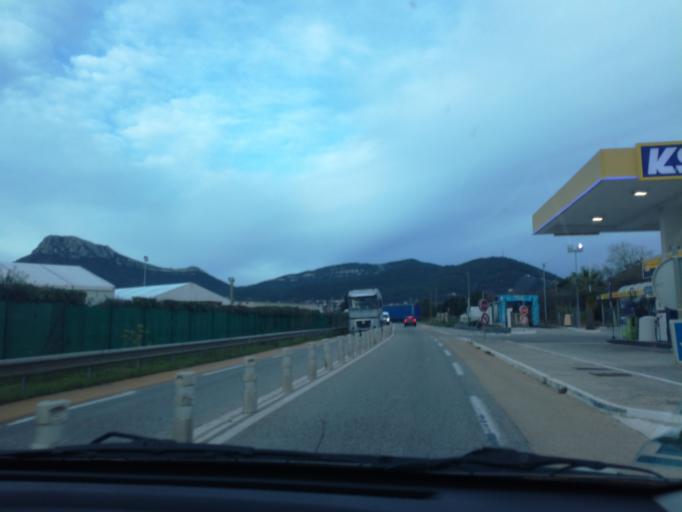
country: FR
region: Provence-Alpes-Cote d'Azur
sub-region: Departement du Var
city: La Crau
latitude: 43.1592
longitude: 6.0642
